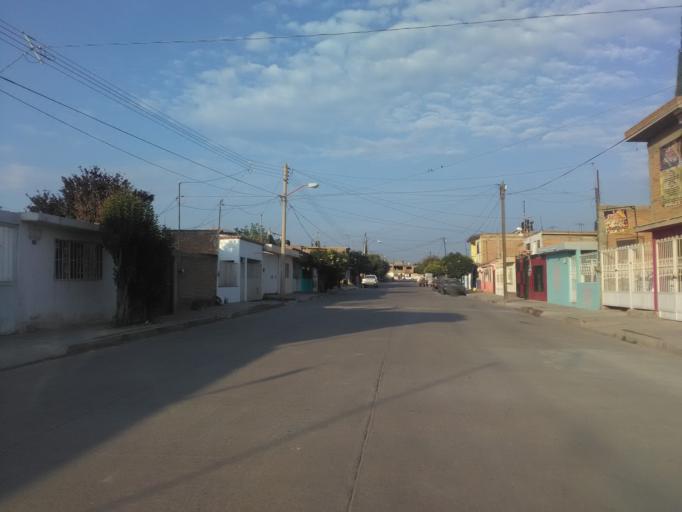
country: MX
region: Durango
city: Victoria de Durango
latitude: 24.0498
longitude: -104.6466
